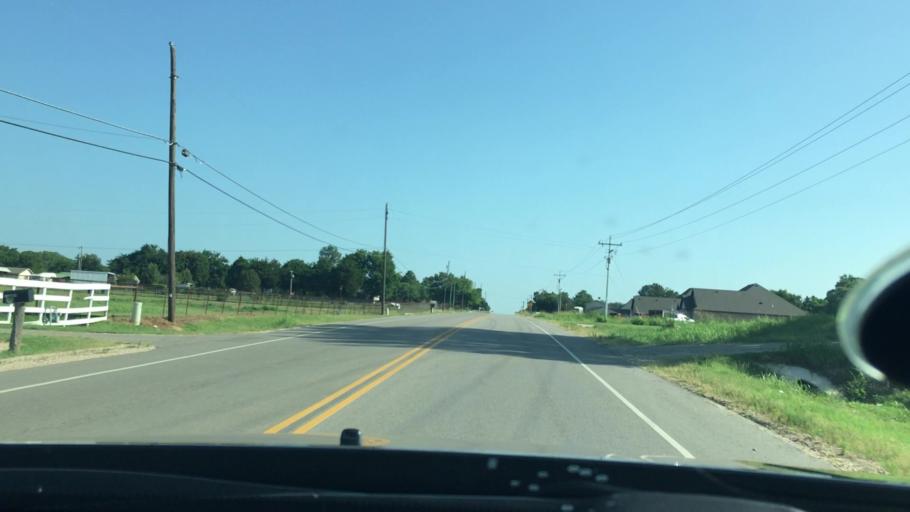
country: US
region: Oklahoma
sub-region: Pontotoc County
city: Ada
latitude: 34.8058
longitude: -96.6523
